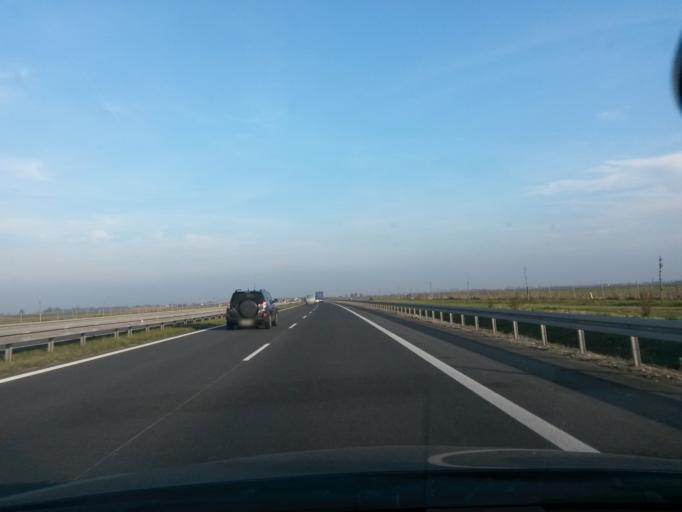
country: PL
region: Lower Silesian Voivodeship
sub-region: Powiat olesnicki
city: Dobroszyce
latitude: 51.2224
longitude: 17.3329
